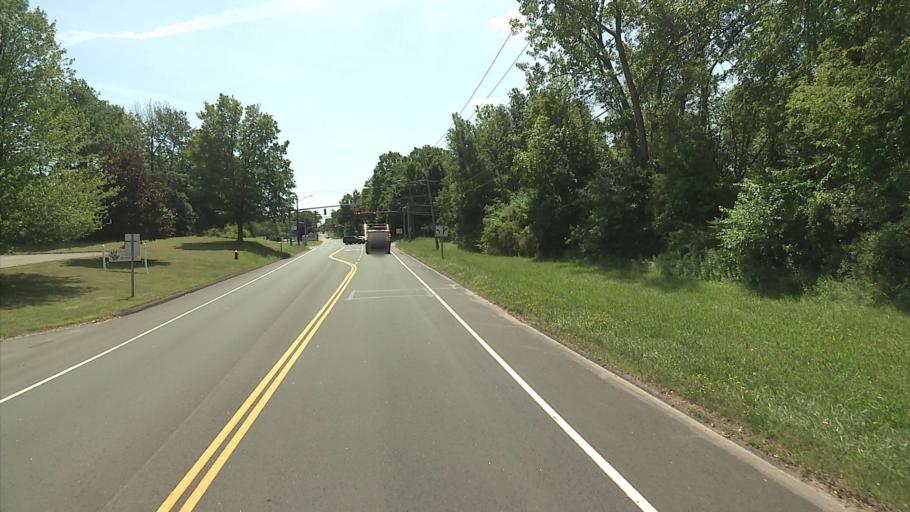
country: US
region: Connecticut
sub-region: Hartford County
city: Kensington
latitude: 41.6172
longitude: -72.7293
